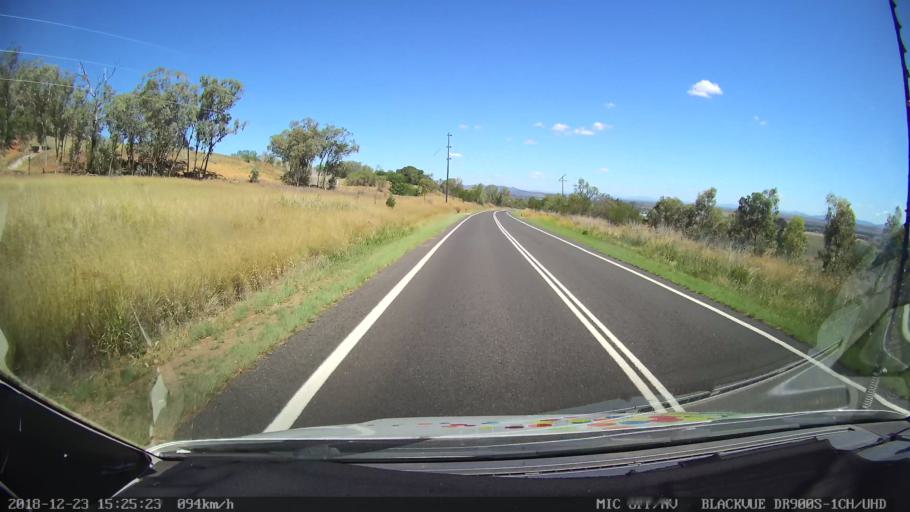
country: AU
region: New South Wales
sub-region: Tamworth Municipality
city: Manilla
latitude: -30.9032
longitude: 150.8305
